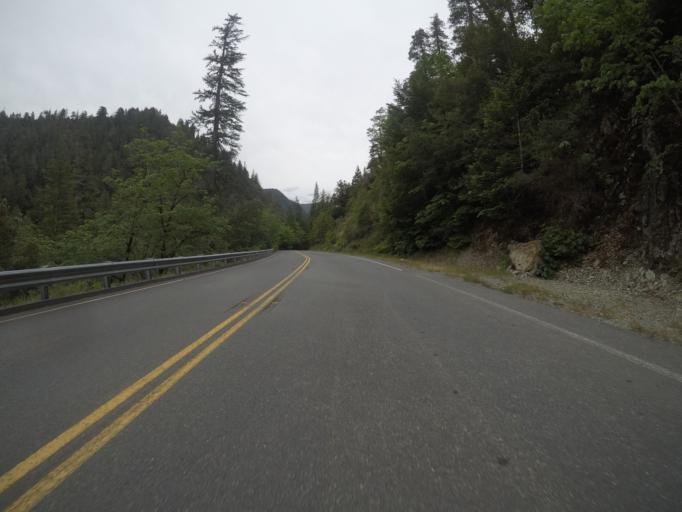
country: US
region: California
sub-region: Del Norte County
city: Bertsch-Oceanview
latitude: 41.7145
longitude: -123.9440
